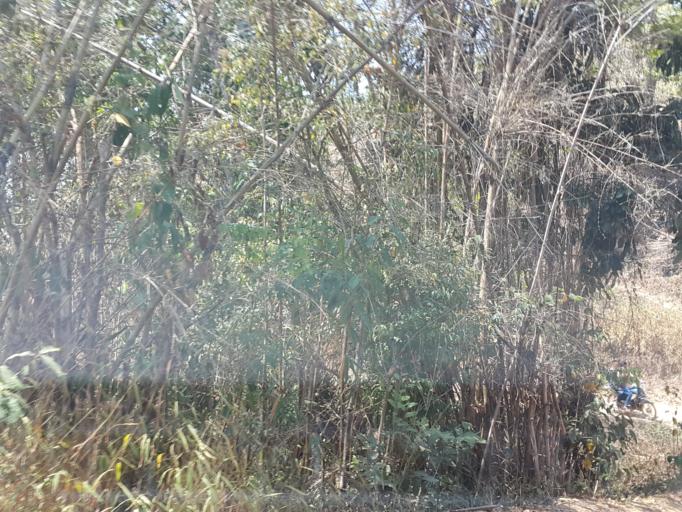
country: TH
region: Chiang Mai
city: Samoeng
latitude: 18.8877
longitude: 98.7817
